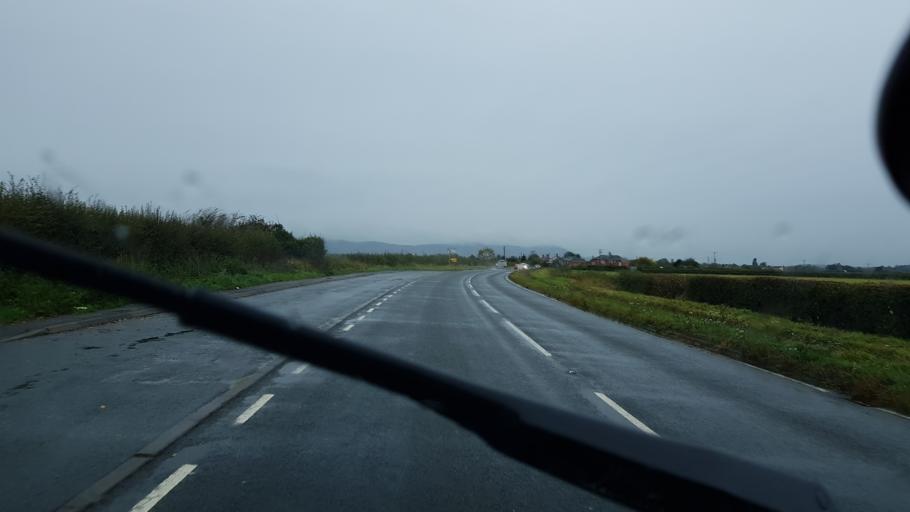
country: GB
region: England
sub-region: Worcestershire
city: Upton upon Severn
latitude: 52.0507
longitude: -2.1810
